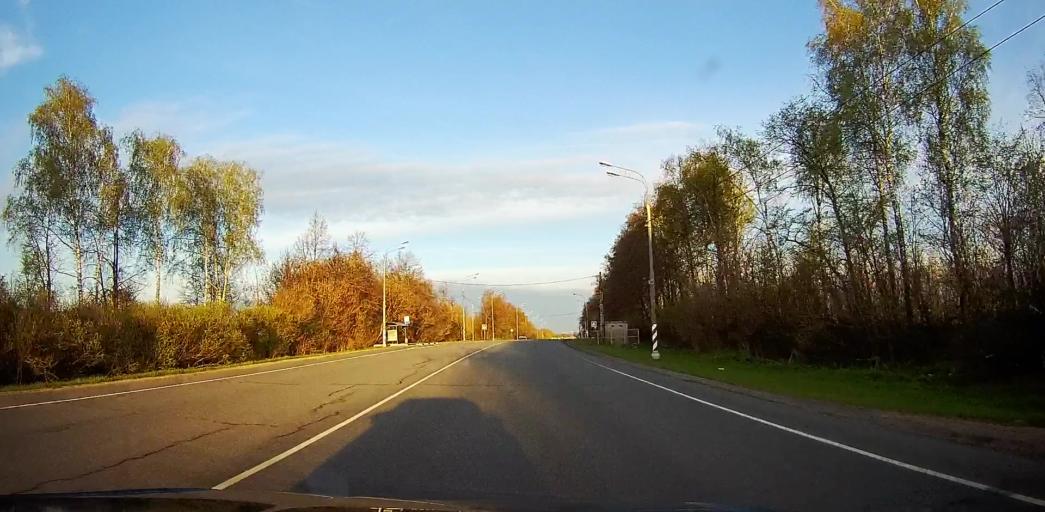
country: RU
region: Moskovskaya
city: Troitskoye
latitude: 55.2231
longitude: 38.5737
